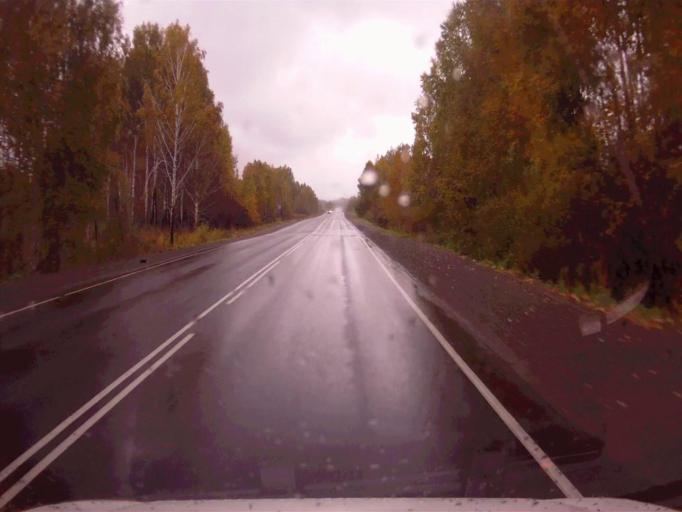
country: RU
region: Chelyabinsk
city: Argayash
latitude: 55.4795
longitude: 60.7585
